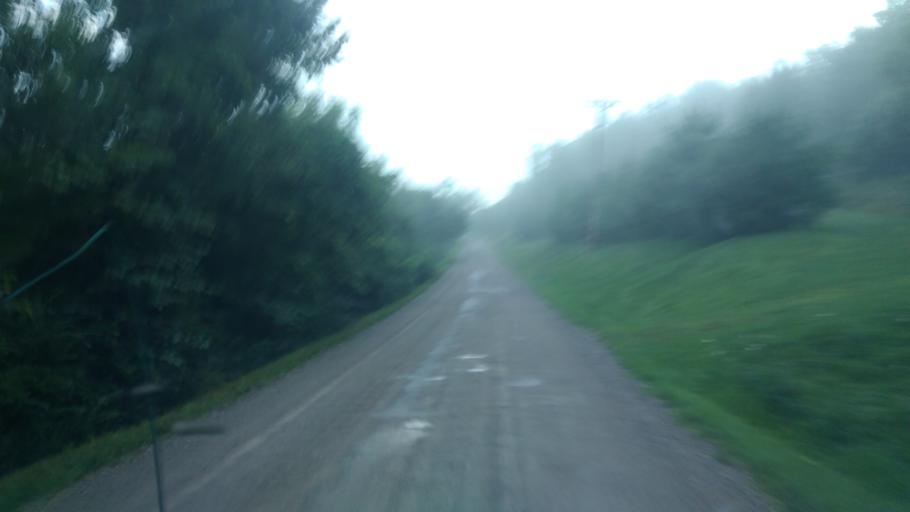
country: US
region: Ohio
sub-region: Guernsey County
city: Byesville
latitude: 40.0080
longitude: -81.3659
